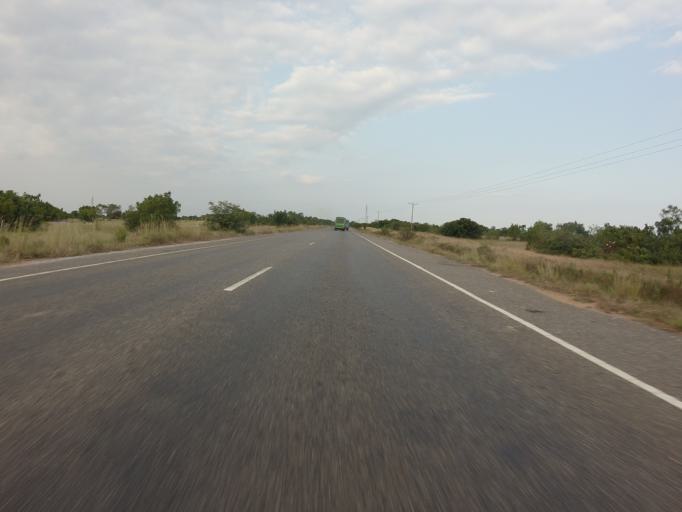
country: GH
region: Volta
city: Anloga
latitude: 6.0897
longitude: 0.5226
